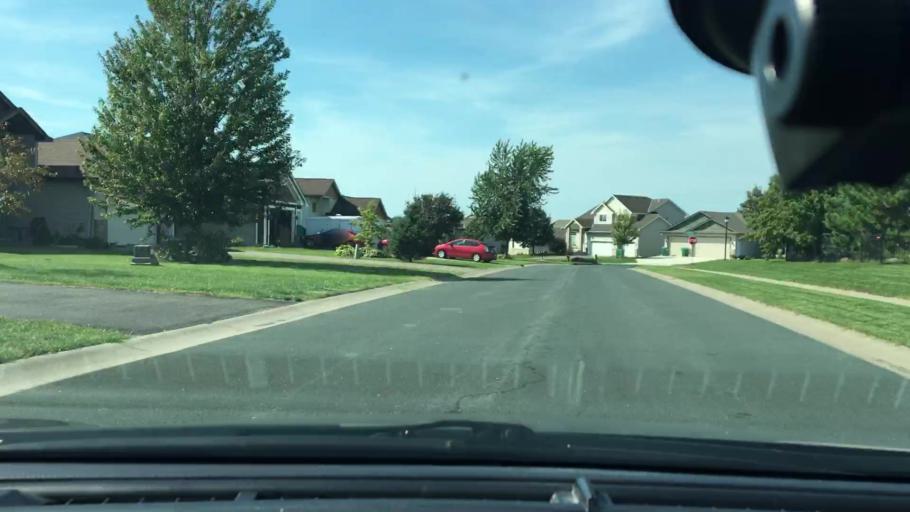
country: US
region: Minnesota
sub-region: Wright County
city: Albertville
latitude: 45.2578
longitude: -93.6565
